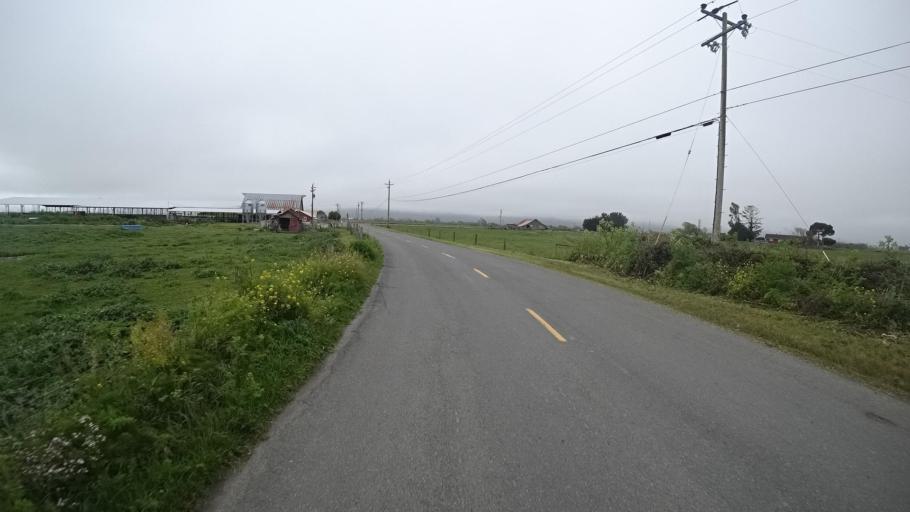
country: US
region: California
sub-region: Humboldt County
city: Fortuna
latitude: 40.6009
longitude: -124.2121
